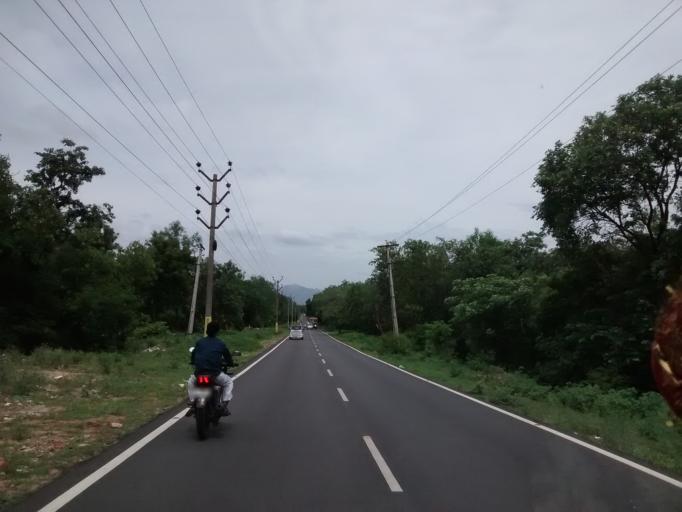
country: IN
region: Andhra Pradesh
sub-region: Chittoor
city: Tirupati
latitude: 13.6376
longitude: 79.3938
